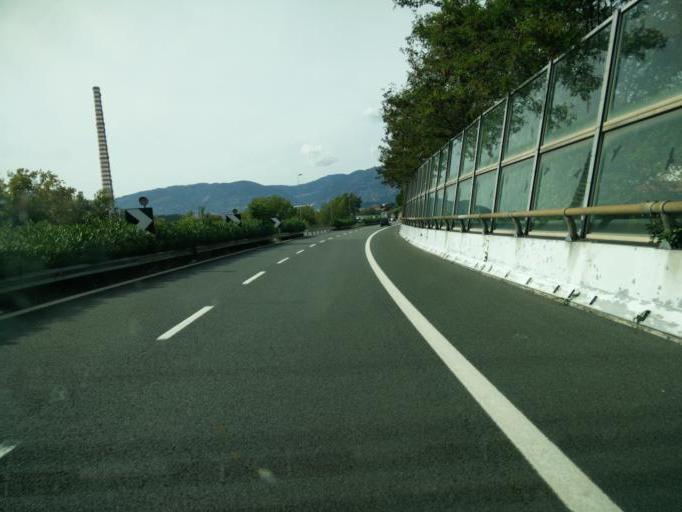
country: IT
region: Liguria
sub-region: Provincia di La Spezia
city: Stazione-Fornola
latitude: 44.1165
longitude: 9.8844
